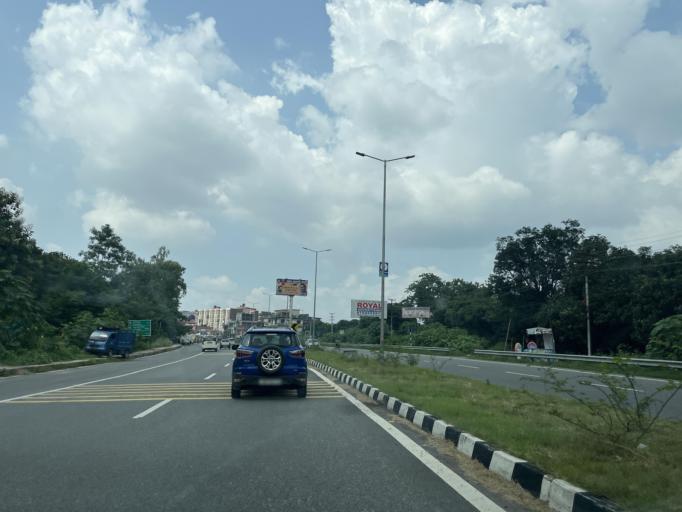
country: IN
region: Uttarakhand
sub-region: Dehradun
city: Raipur
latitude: 30.2685
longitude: 78.0806
